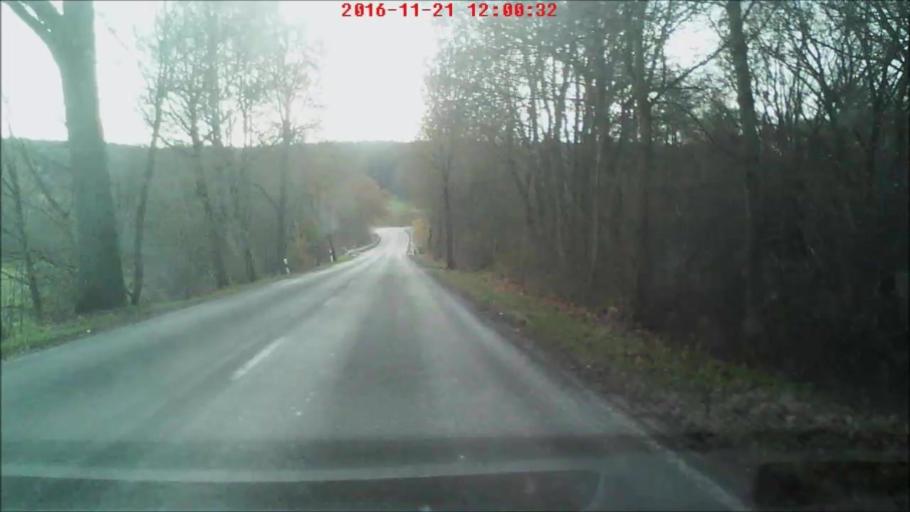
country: DE
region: Thuringia
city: Schleusingen
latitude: 50.5005
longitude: 10.7416
